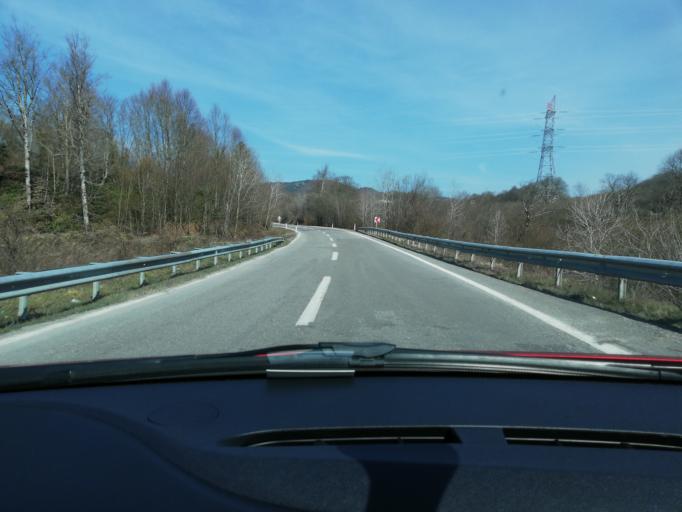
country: TR
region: Bartin
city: Amasra
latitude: 41.7071
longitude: 32.3918
